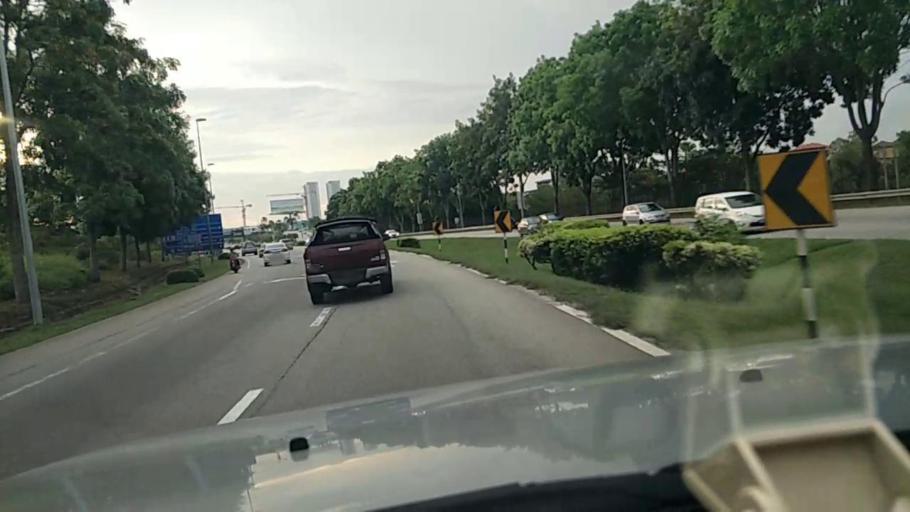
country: MY
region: Selangor
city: Shah Alam
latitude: 3.1024
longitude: 101.4736
